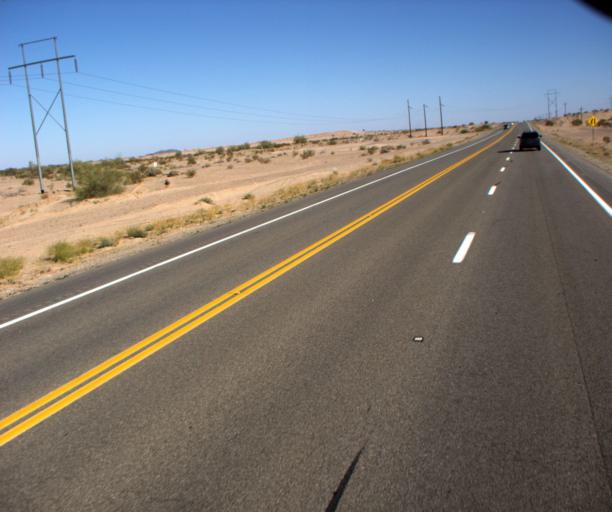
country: US
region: Arizona
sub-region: Yuma County
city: Fortuna Foothills
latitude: 32.8020
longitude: -114.3806
